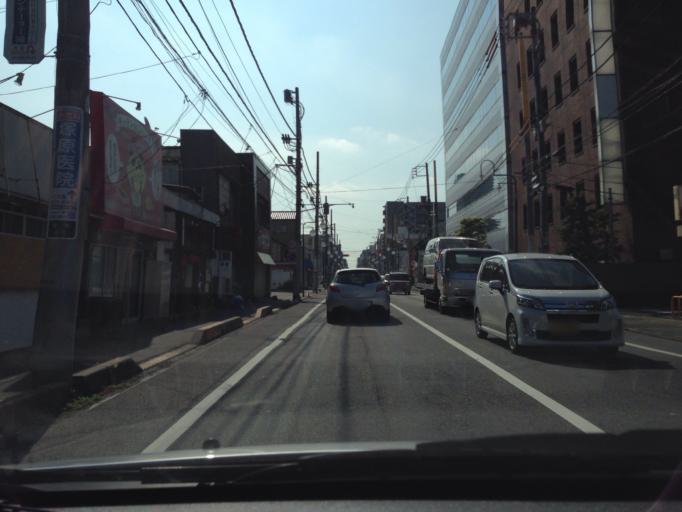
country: JP
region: Ibaraki
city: Naka
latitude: 36.0800
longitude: 140.1970
